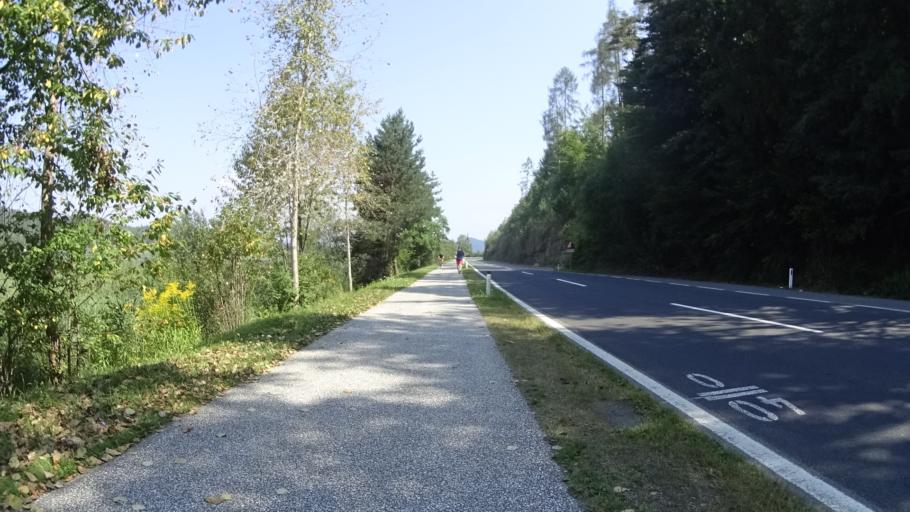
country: AT
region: Carinthia
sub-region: Politischer Bezirk Volkermarkt
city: Sittersdorf
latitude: 46.5608
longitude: 14.6239
